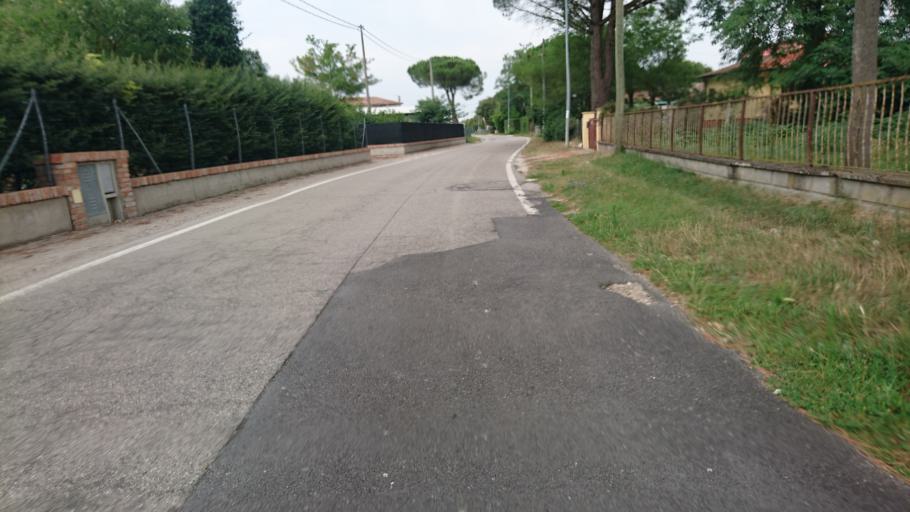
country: IT
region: Veneto
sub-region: Provincia di Rovigo
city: Rosolina
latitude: 45.0789
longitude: 12.2301
